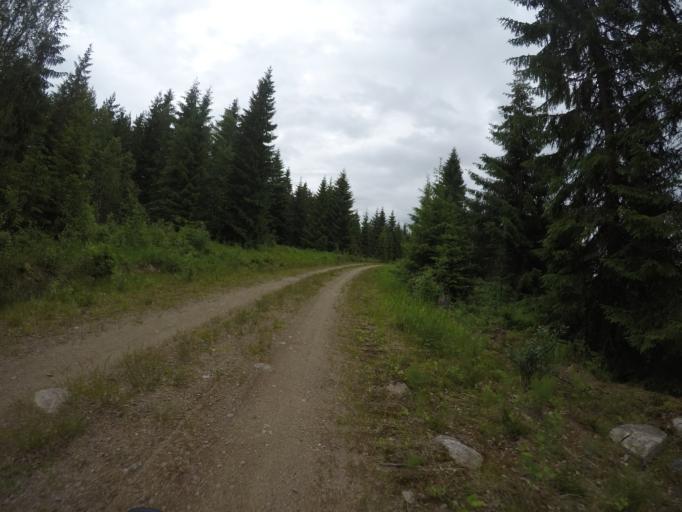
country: SE
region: Dalarna
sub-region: Ludvika Kommun
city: Abborrberget
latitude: 60.0615
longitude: 14.5637
